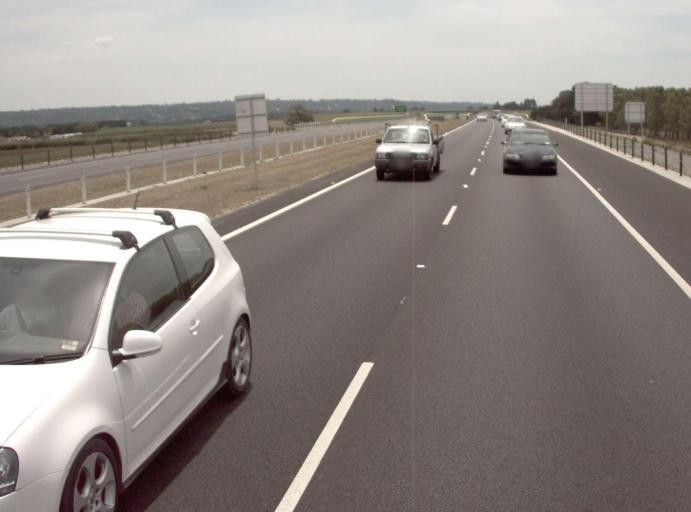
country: AU
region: Victoria
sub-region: Mornington Peninsula
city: Moorooduc
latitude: -38.2410
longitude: 145.1231
